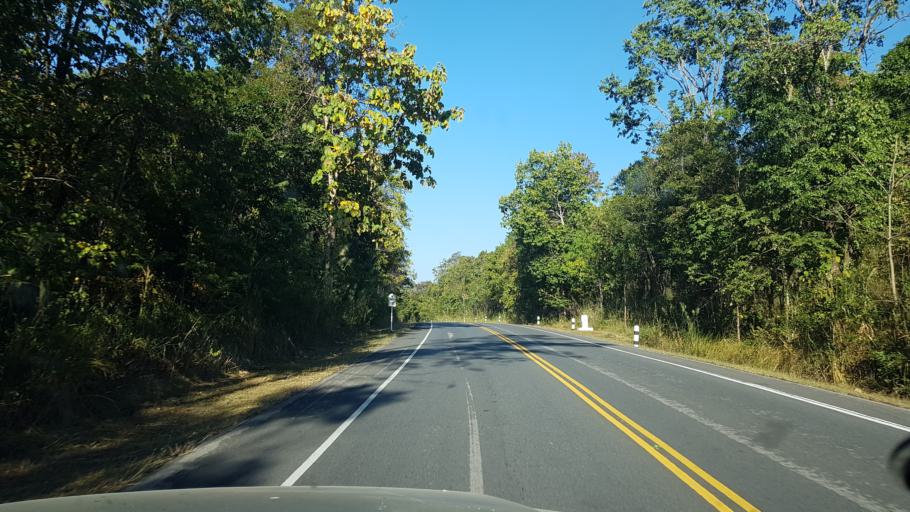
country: TH
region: Phetchabun
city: Lom Sak
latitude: 16.7401
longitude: 101.4444
